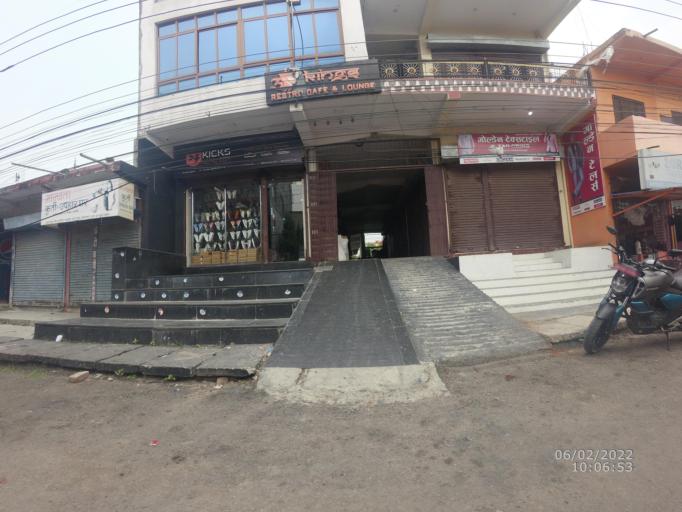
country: NP
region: Western Region
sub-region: Lumbini Zone
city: Bhairahawa
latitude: 27.5076
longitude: 83.4532
